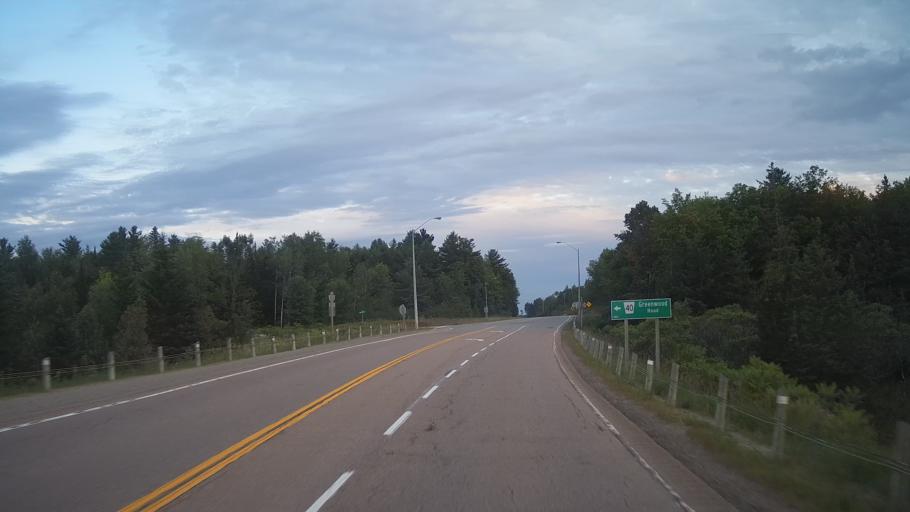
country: CA
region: Ontario
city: Pembroke
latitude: 45.7461
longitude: -77.0054
